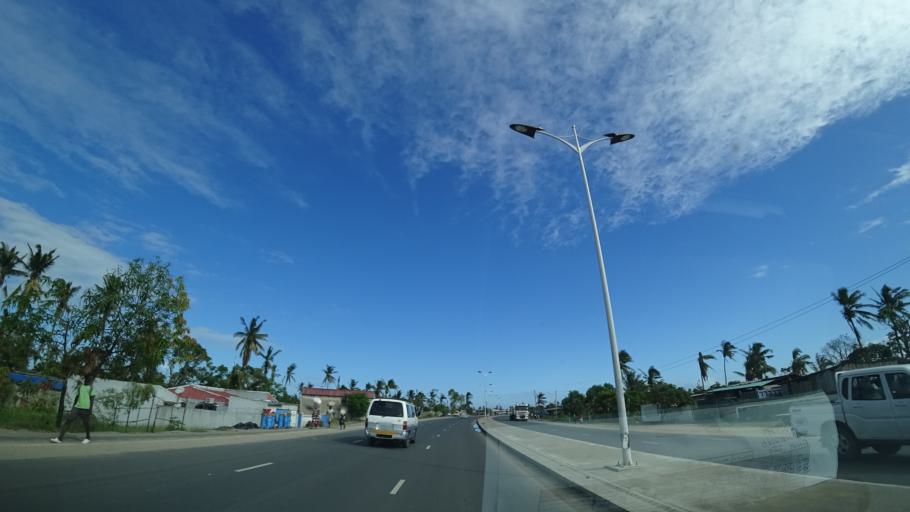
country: MZ
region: Sofala
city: Beira
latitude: -19.7735
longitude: 34.8834
